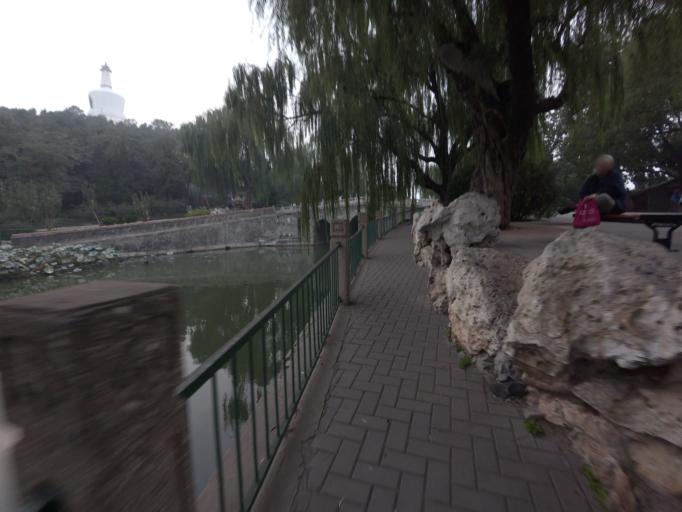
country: CN
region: Beijing
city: Jingshan
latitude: 39.9242
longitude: 116.3846
